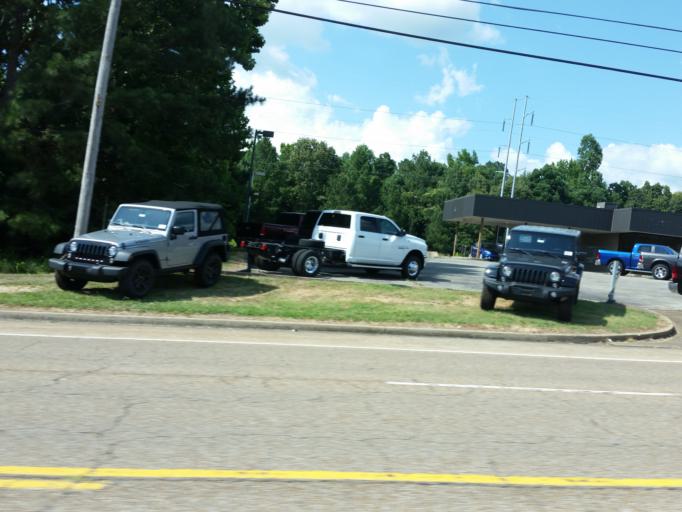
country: US
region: Tennessee
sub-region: Henderson County
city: Lexington
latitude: 35.6419
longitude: -88.3800
